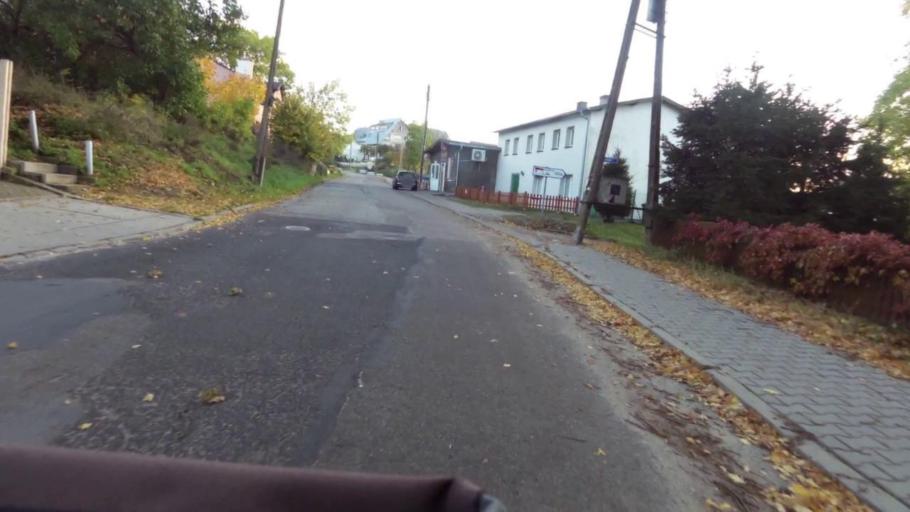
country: PL
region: West Pomeranian Voivodeship
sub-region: Powiat kamienski
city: Miedzyzdroje
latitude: 53.8704
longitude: 14.4276
